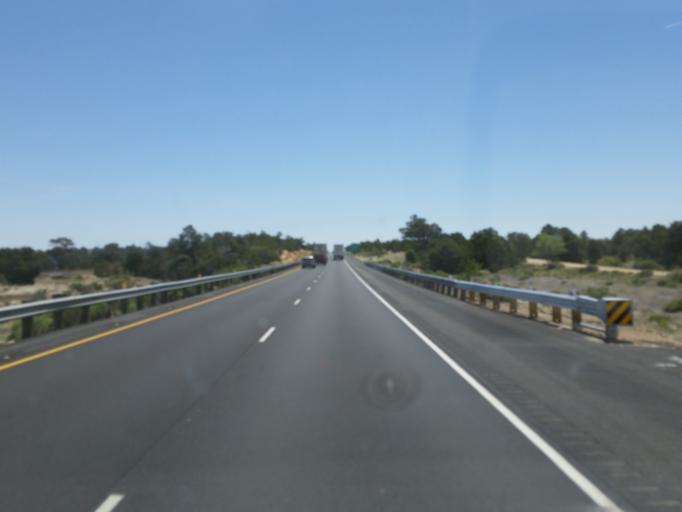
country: US
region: Arizona
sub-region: Coconino County
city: Flagstaff
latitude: 35.2038
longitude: -111.4902
